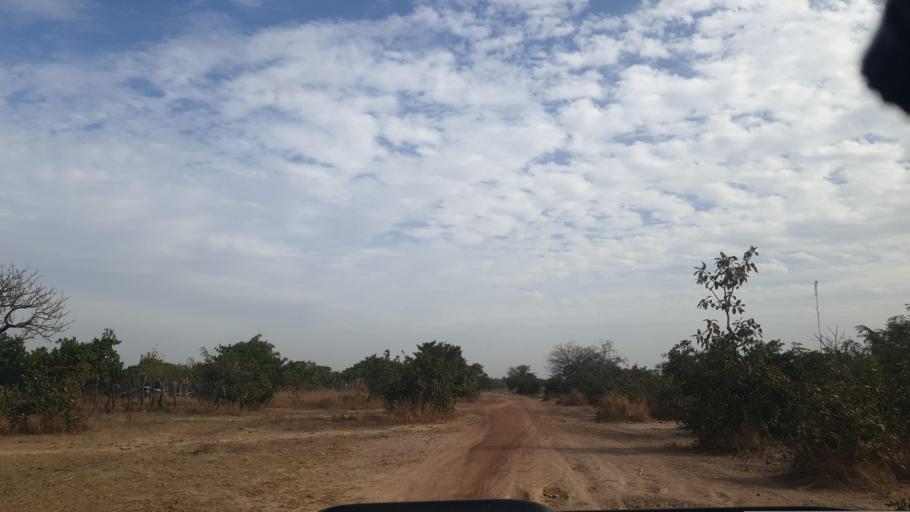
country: ML
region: Sikasso
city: Yanfolila
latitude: 11.4100
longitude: -8.0074
